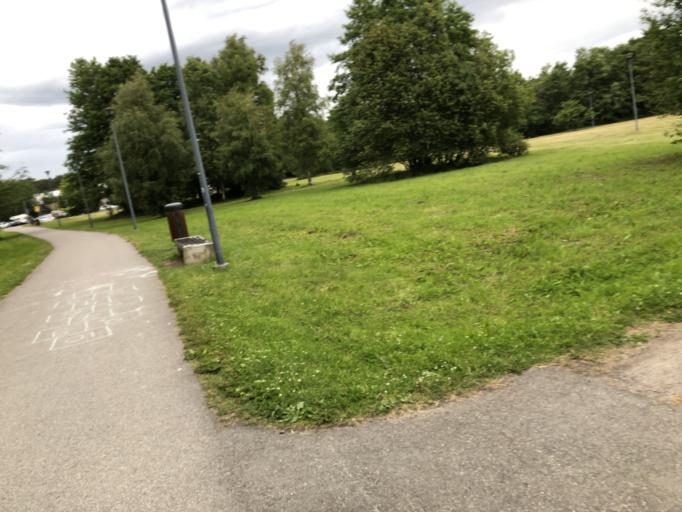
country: EE
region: Harju
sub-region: Viimsi vald
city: Viimsi
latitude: 59.4603
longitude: 24.8298
